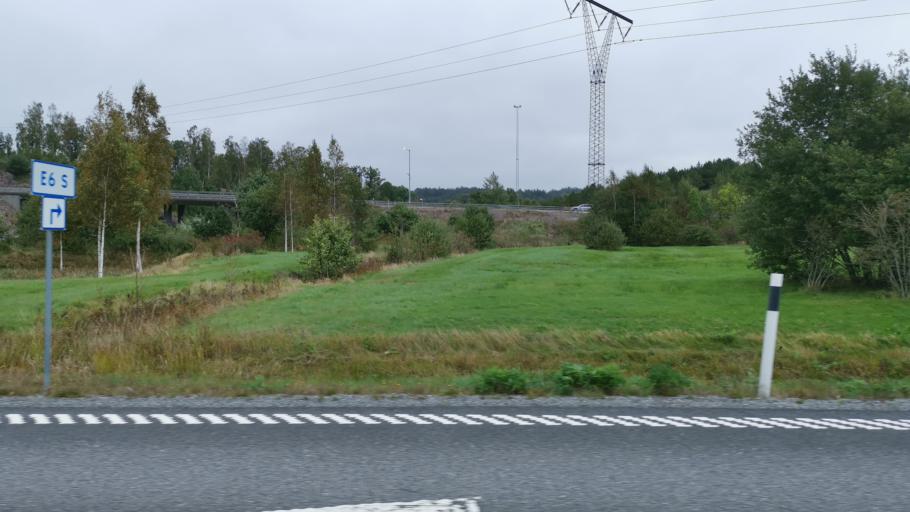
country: SE
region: Vaestra Goetaland
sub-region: Lysekils Kommun
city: Brastad
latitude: 58.5638
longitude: 11.4745
